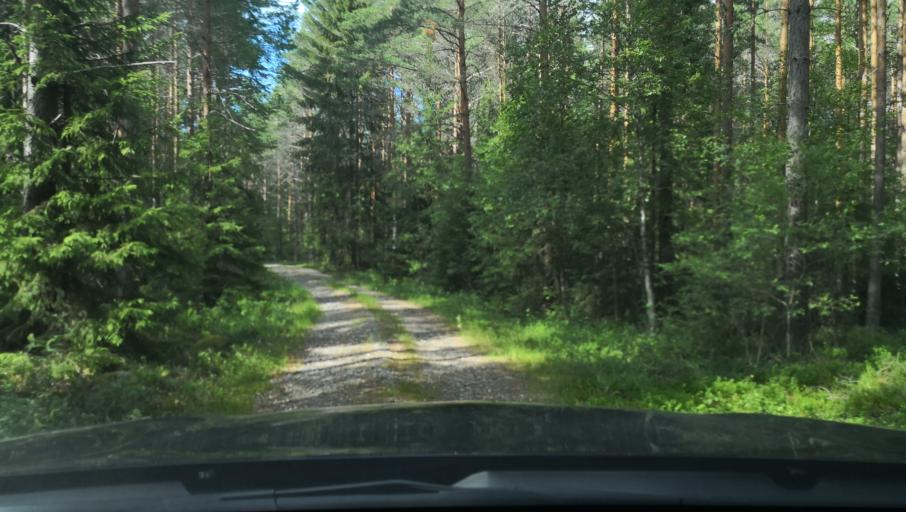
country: SE
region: Vaestmanland
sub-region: Hallstahammars Kommun
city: Hallstahammar
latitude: 59.6492
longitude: 16.0979
